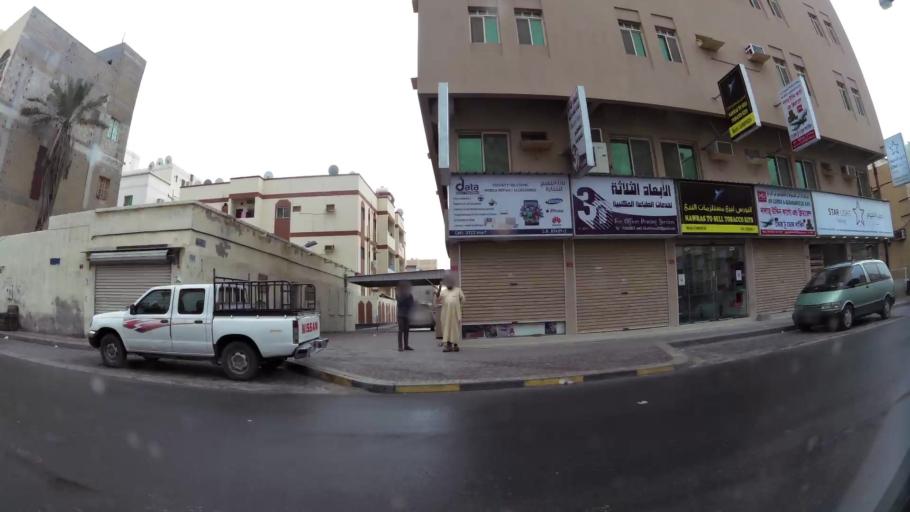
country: BH
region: Northern
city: Ar Rifa'
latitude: 26.1259
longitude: 50.5674
